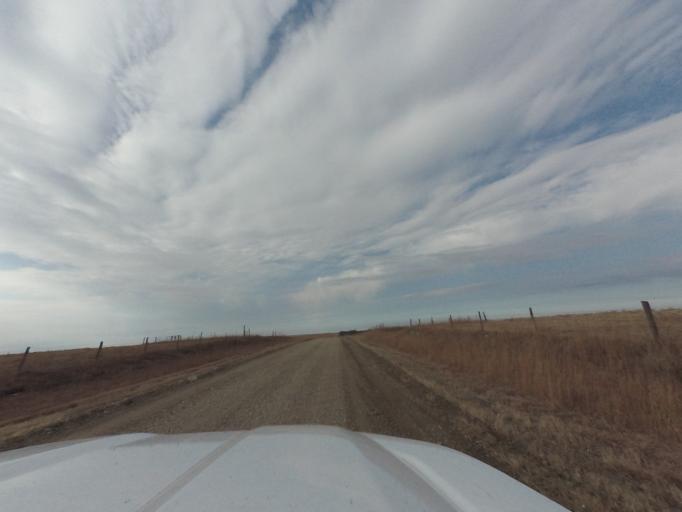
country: US
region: Kansas
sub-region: Chase County
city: Cottonwood Falls
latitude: 38.2171
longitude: -96.7008
